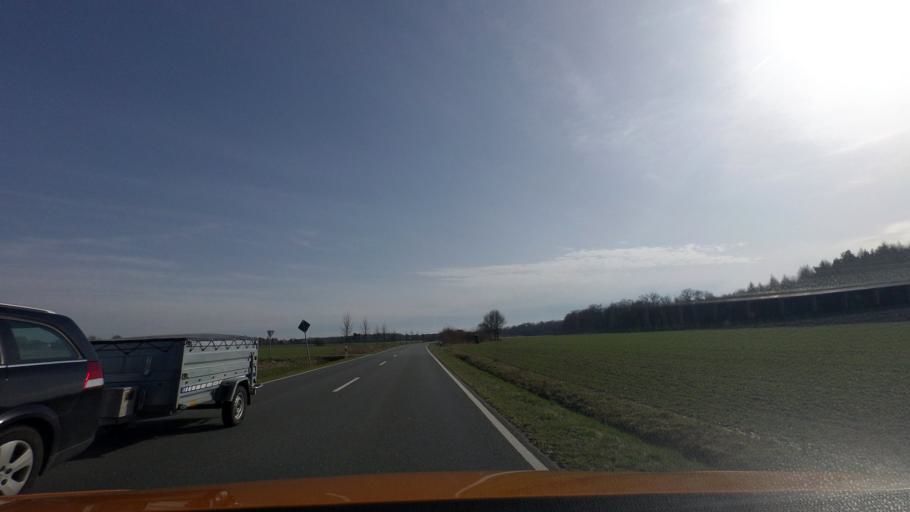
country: DE
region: Lower Saxony
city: Wiedensahl
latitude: 52.3729
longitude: 9.1062
